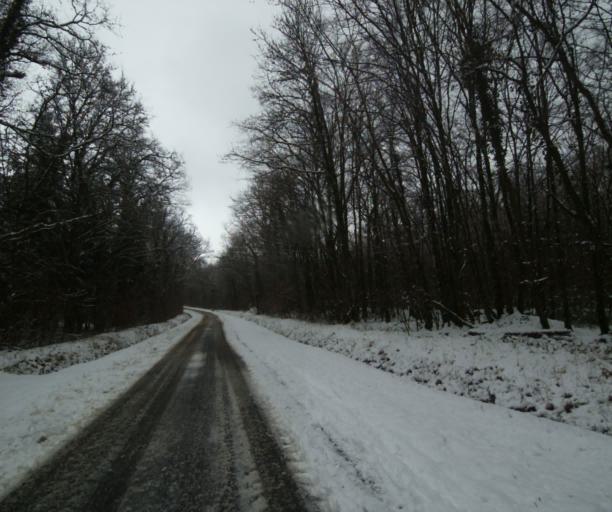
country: FR
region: Champagne-Ardenne
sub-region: Departement de la Haute-Marne
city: Wassy
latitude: 48.4555
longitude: 4.9408
